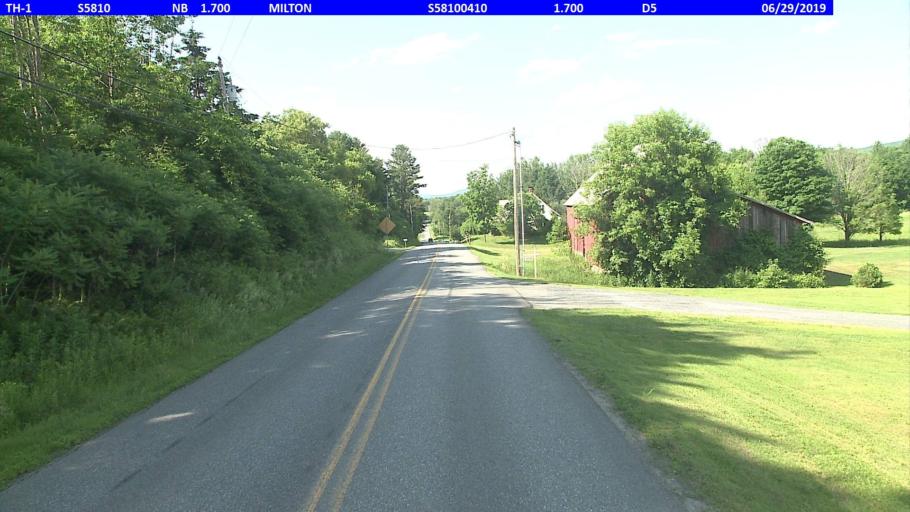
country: US
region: Vermont
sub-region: Chittenden County
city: Milton
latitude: 44.6058
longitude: -73.1246
